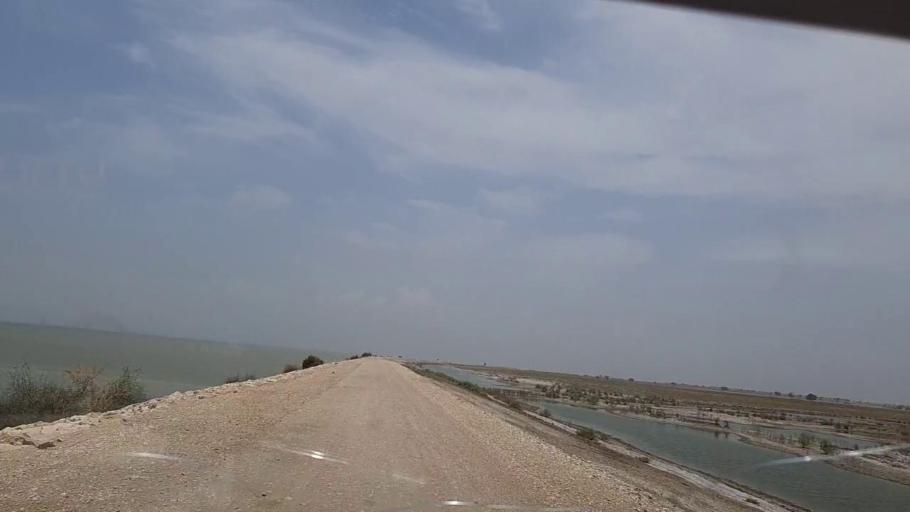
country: PK
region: Sindh
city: Sehwan
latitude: 26.4196
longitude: 67.7333
